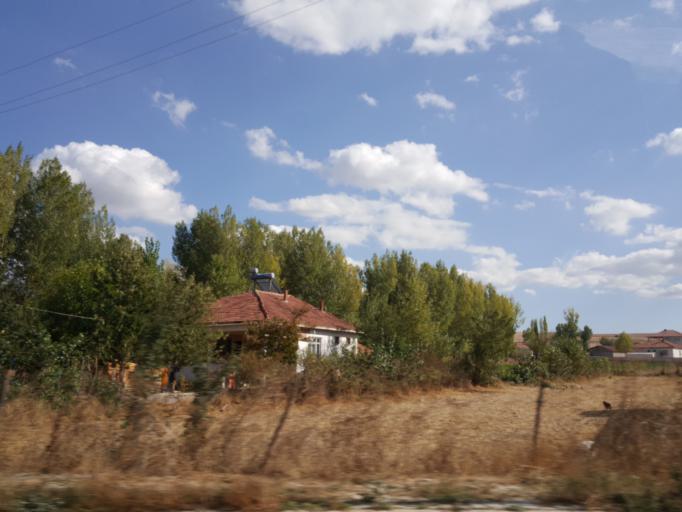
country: TR
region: Tokat
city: Sulusaray
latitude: 39.9882
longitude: 36.0791
